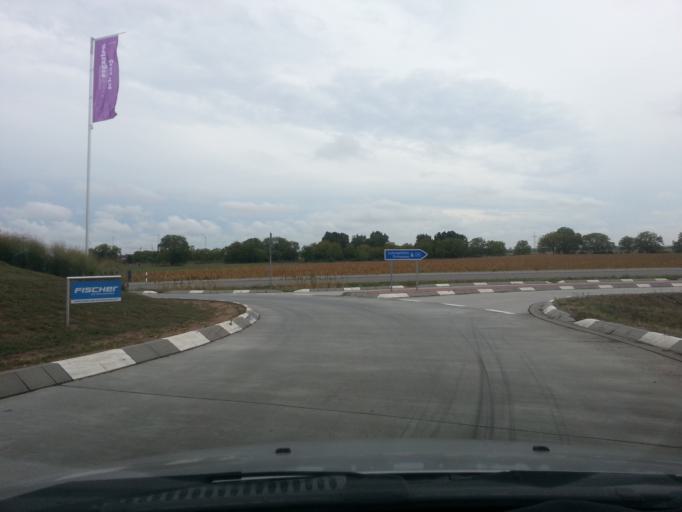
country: DE
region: Rheinland-Pfalz
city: Offenbach an der Queich
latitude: 49.1943
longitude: 8.1522
